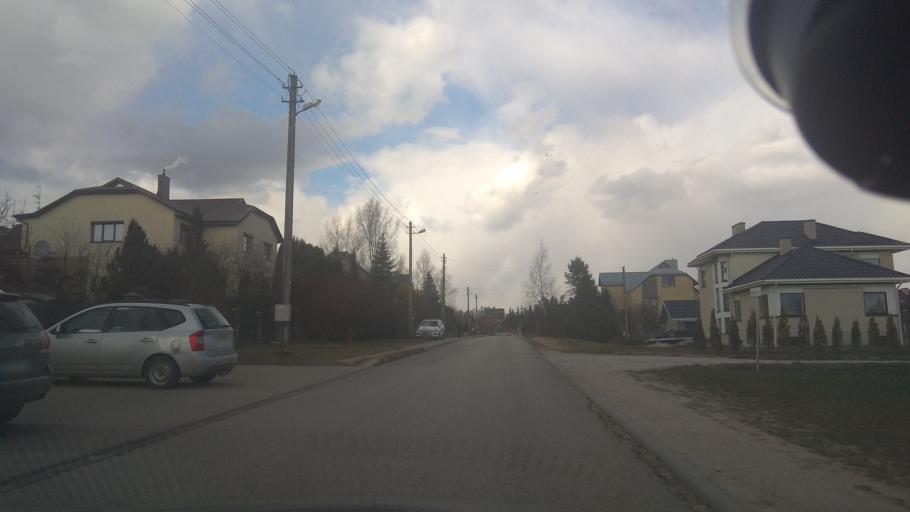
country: LT
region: Vilnius County
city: Pasilaiciai
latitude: 54.7371
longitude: 25.2020
